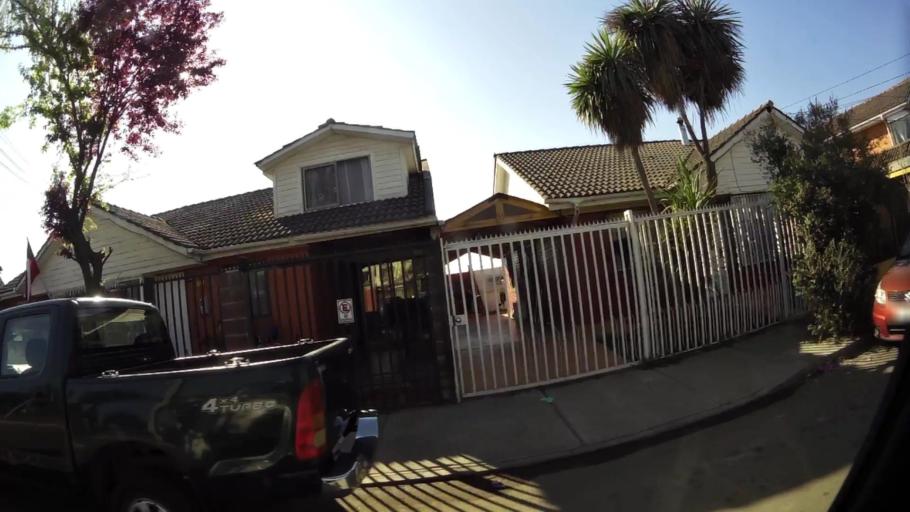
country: CL
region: Santiago Metropolitan
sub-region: Provincia de Santiago
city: Lo Prado
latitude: -33.4907
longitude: -70.7851
